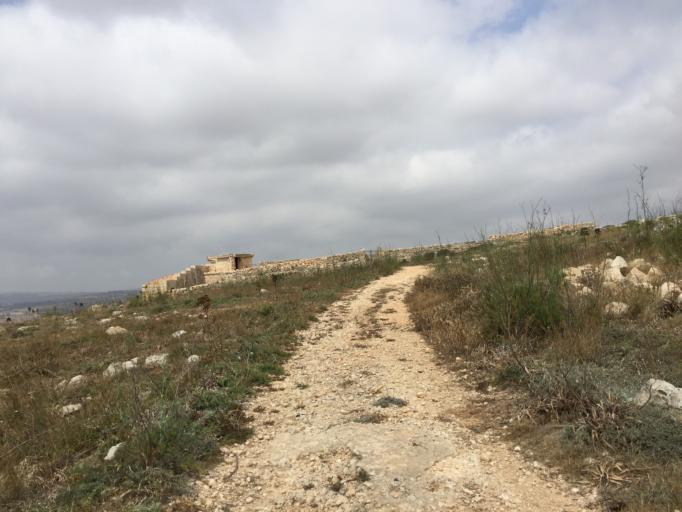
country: MT
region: L-Imgarr
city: Imgarr
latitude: 35.9026
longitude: 14.3463
